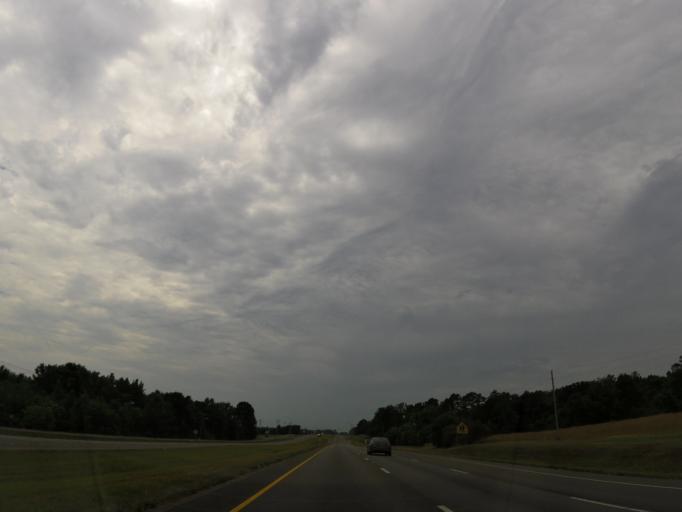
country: US
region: Alabama
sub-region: Jackson County
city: Scottsboro
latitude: 34.6779
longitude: -86.0023
